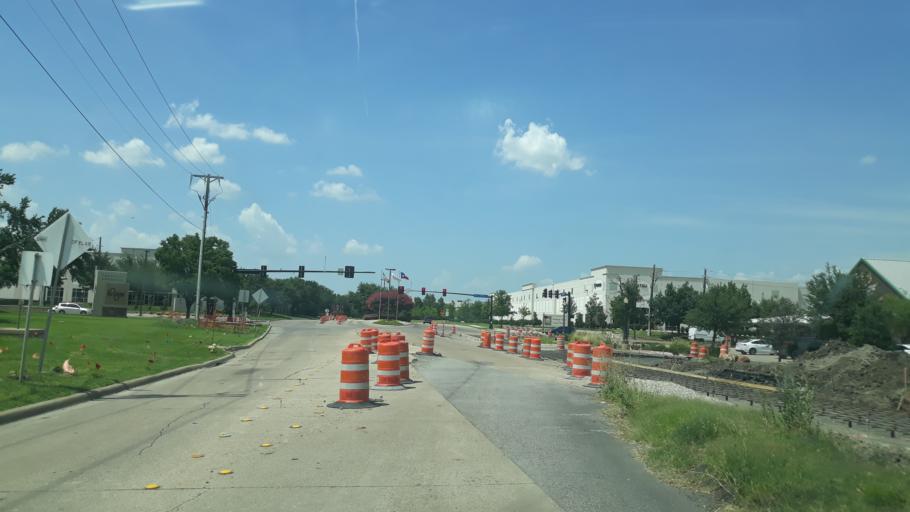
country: US
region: Texas
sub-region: Dallas County
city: Coppell
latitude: 32.9537
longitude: -97.0108
